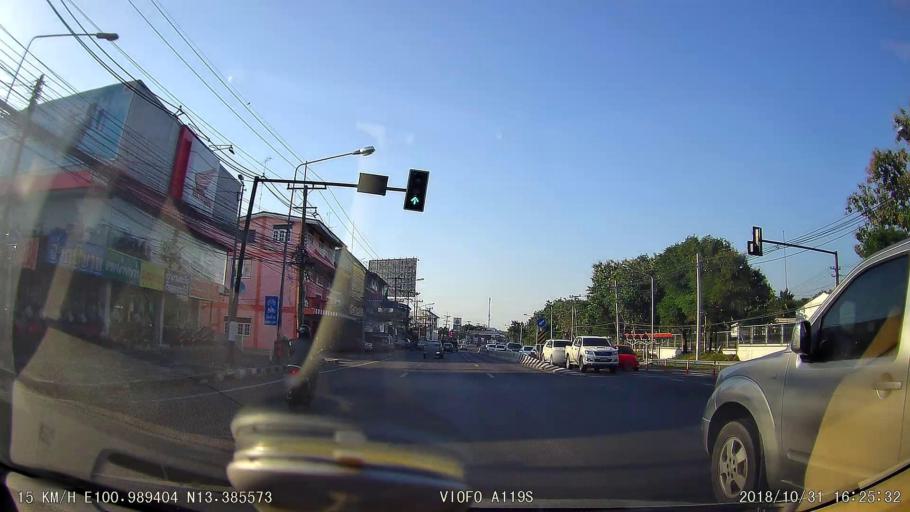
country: TH
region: Chon Buri
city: Chon Buri
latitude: 13.3857
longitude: 100.9893
